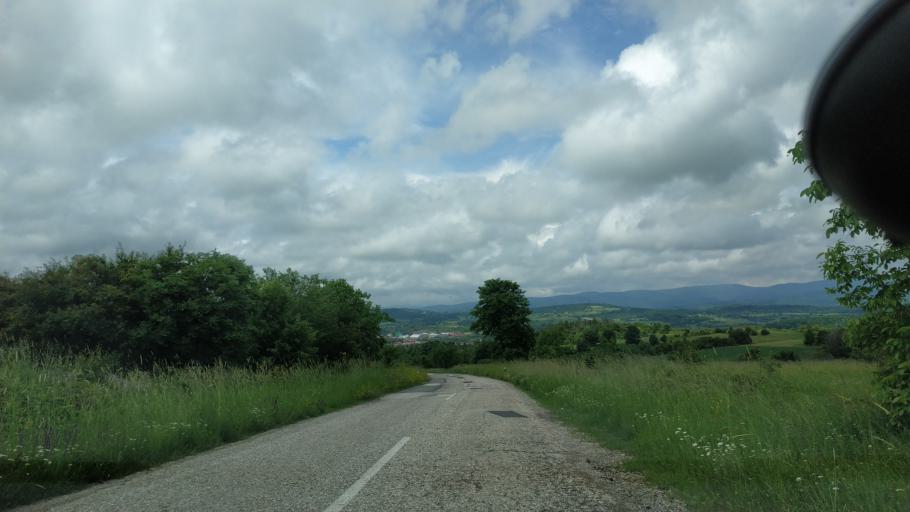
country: RS
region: Central Serbia
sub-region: Zajecarski Okrug
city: Boljevac
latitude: 43.8335
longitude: 21.9801
